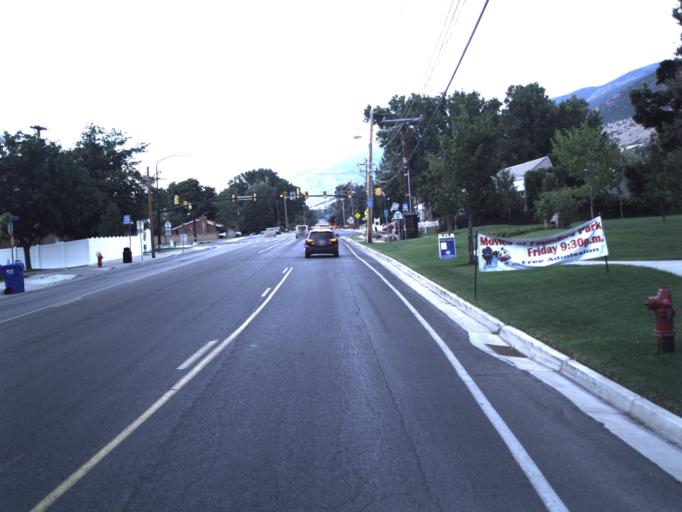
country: US
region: Utah
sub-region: Davis County
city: Centerville
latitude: 40.9202
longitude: -111.8789
